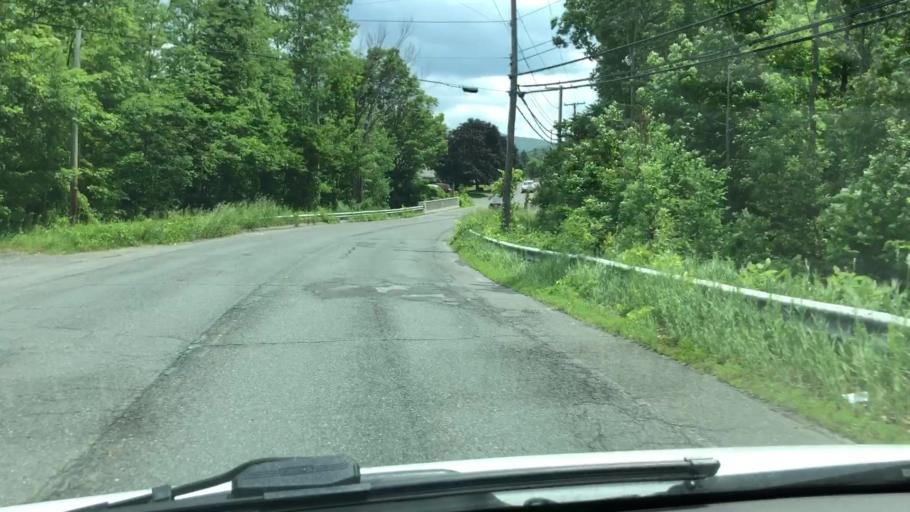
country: US
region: Massachusetts
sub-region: Berkshire County
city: Adams
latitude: 42.5907
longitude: -73.1144
